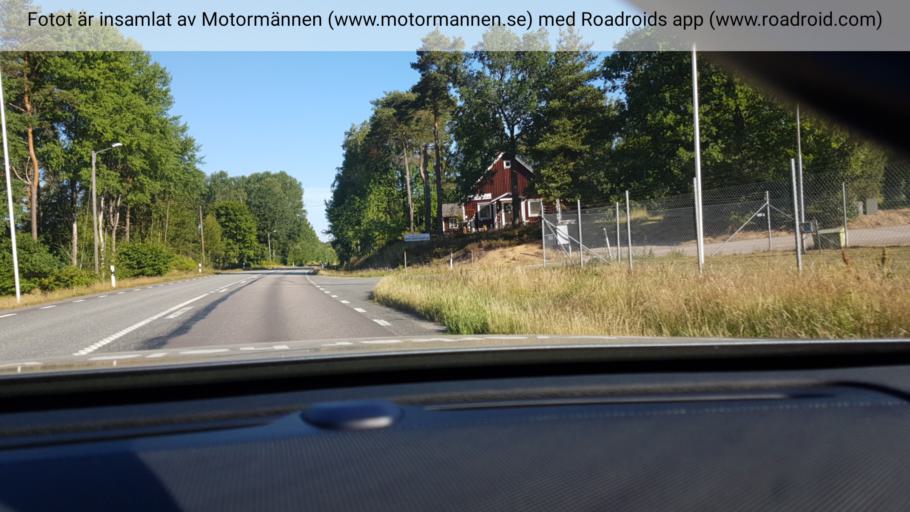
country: SE
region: Kronoberg
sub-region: Markaryds Kommun
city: Markaryd
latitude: 56.4388
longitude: 13.6085
